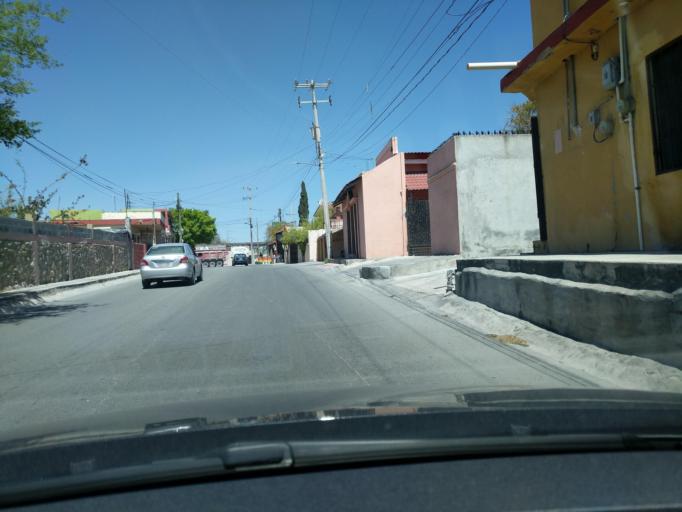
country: MX
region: Nuevo Leon
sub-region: Apodaca
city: Artemio Trevino
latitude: 25.8157
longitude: -100.1521
